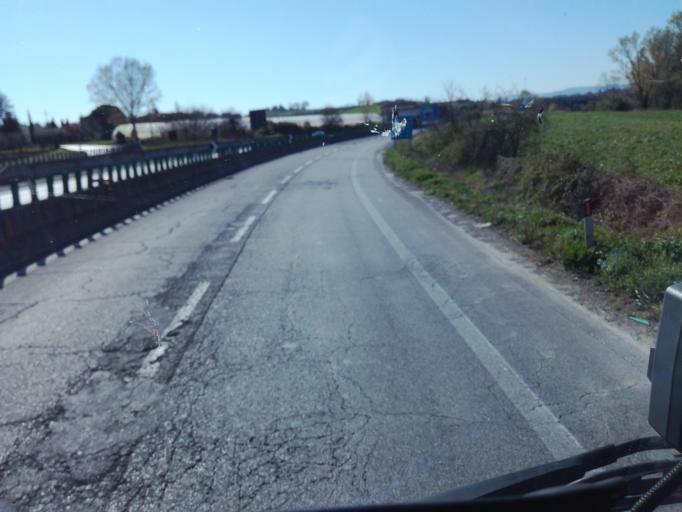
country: IT
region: Umbria
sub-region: Provincia di Perugia
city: Via Lippia
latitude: 43.1059
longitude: 12.4758
